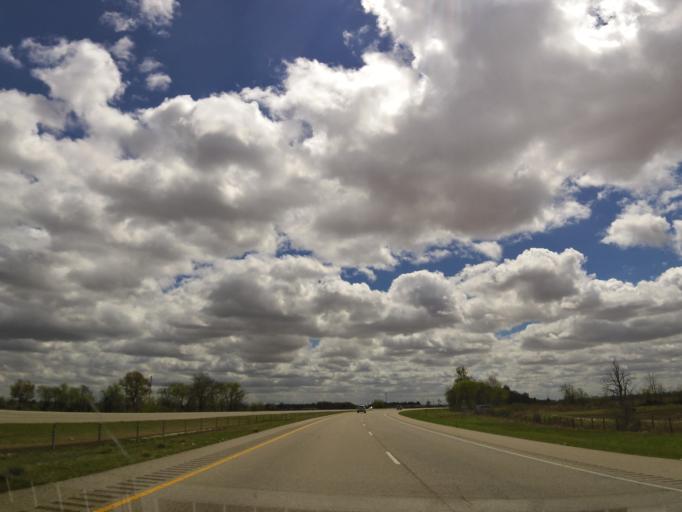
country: US
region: Arkansas
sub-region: Craighead County
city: Bay
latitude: 35.6944
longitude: -90.5538
